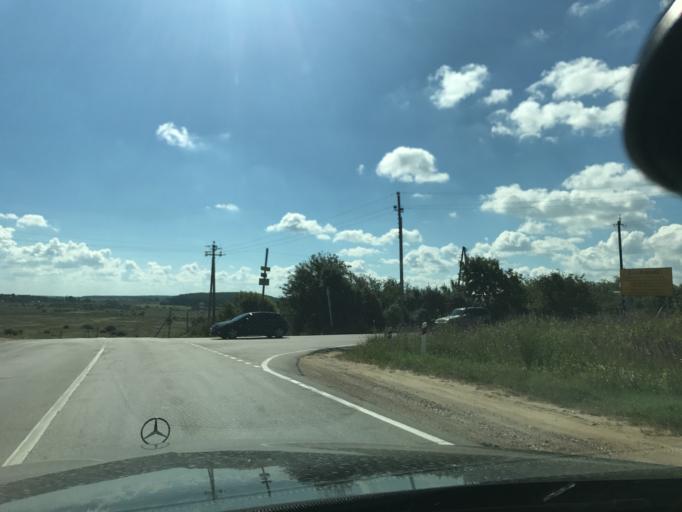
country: RU
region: Vladimir
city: Stavrovo
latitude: 56.1229
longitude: 39.9999
